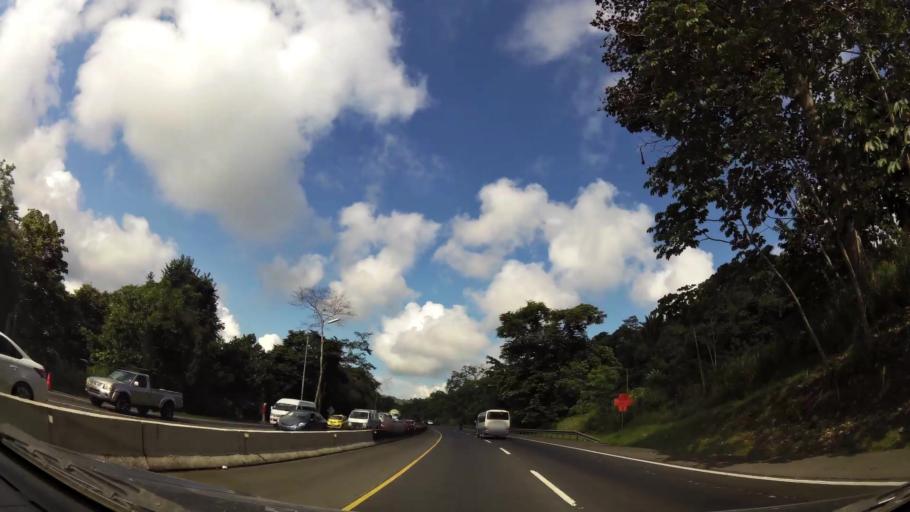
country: PA
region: Panama
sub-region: Distrito Arraijan
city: Arraijan
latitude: 8.9573
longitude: -79.6040
